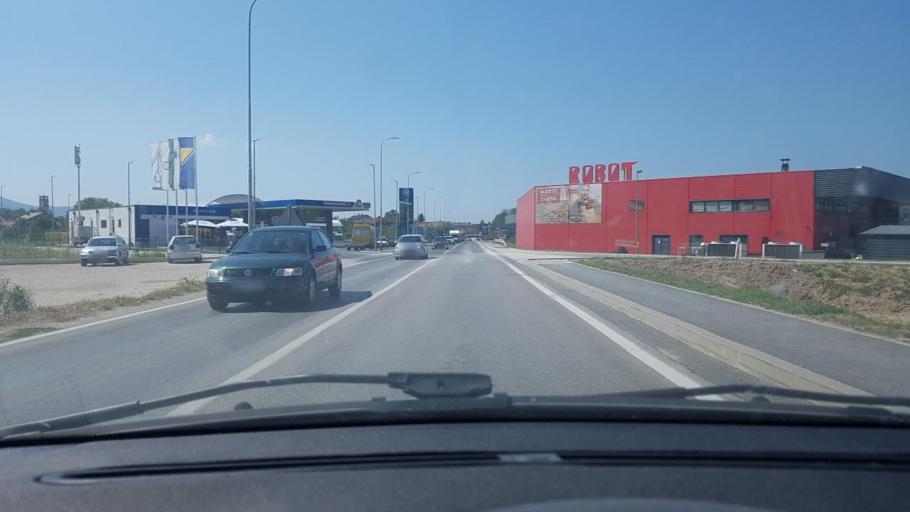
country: BA
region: Federation of Bosnia and Herzegovina
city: Bihac
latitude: 44.8116
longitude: 15.8812
